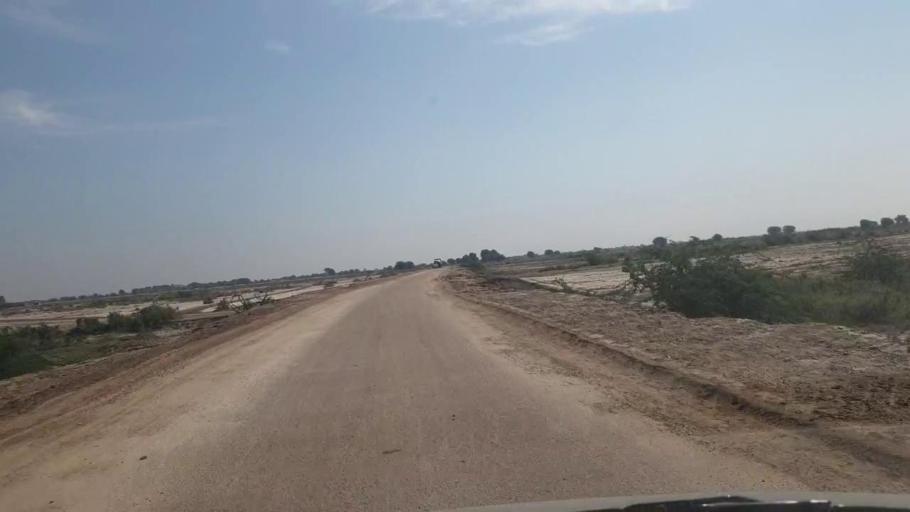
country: PK
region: Sindh
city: Digri
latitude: 24.9747
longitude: 69.1217
